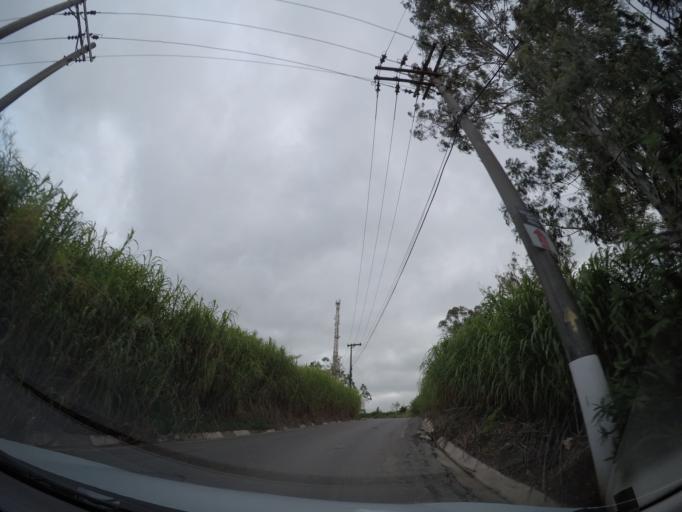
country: BR
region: Sao Paulo
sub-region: Vinhedo
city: Vinhedo
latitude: -23.0694
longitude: -47.0325
